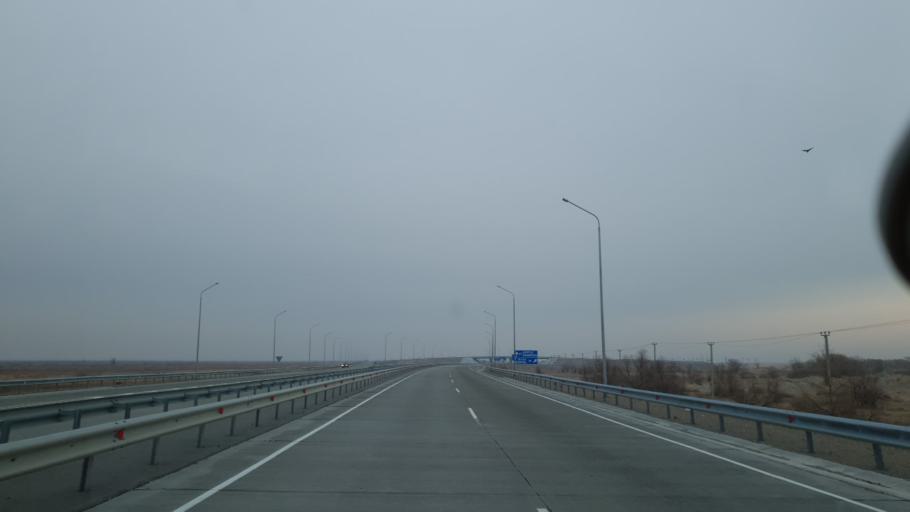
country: KZ
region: Almaty Oblysy
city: Zharkent
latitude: 44.0097
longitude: 79.6672
